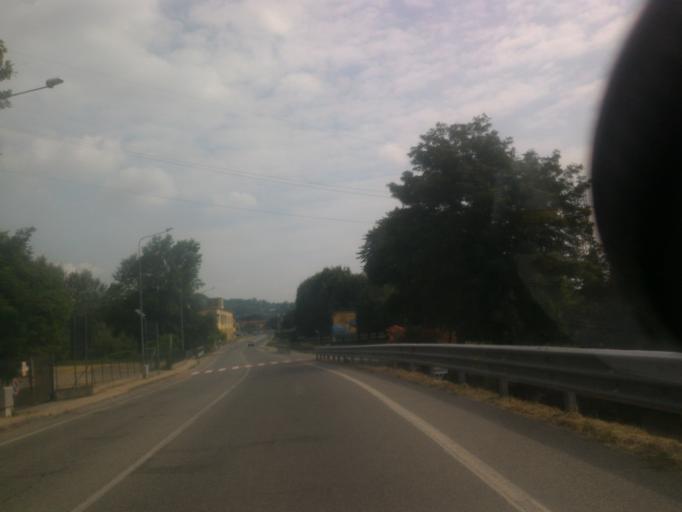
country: IT
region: Piedmont
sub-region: Provincia di Torino
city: San Secondo di Pinerolo
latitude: 44.8753
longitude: 7.3111
